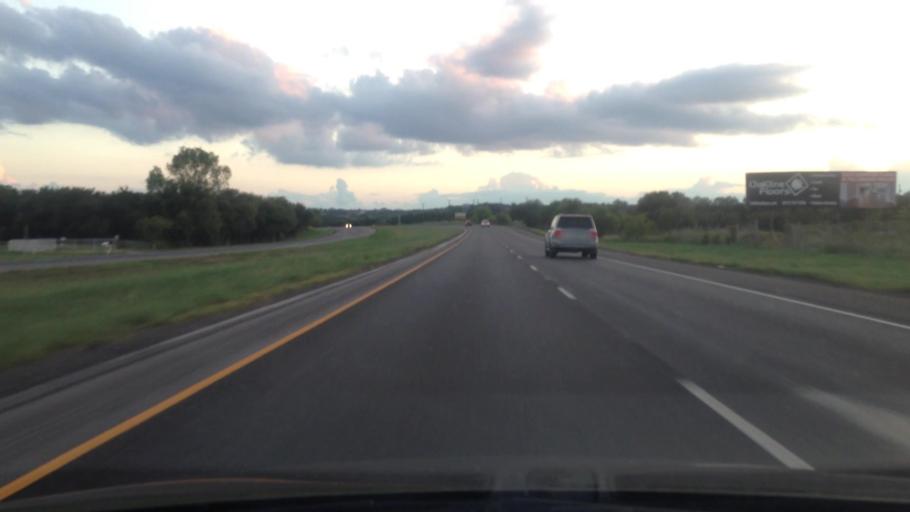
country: US
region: Texas
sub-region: Parker County
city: Aledo
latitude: 32.5881
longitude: -97.5918
